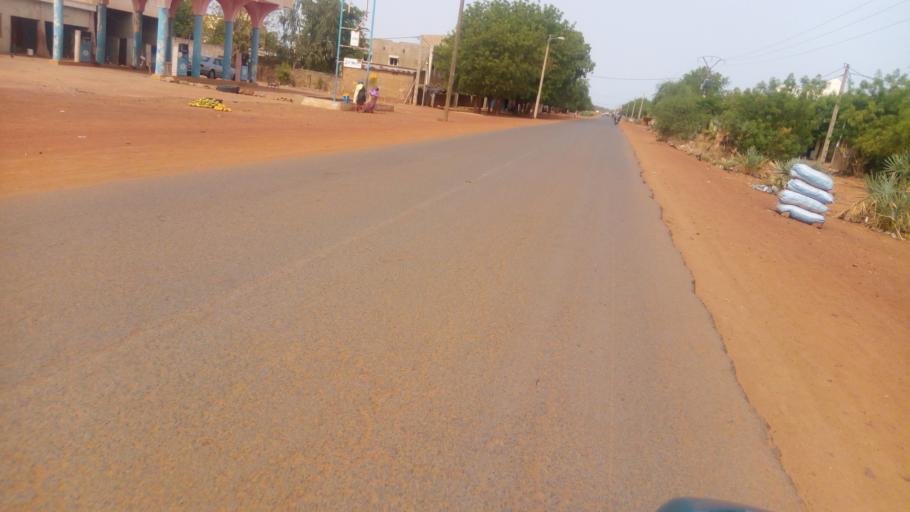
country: ML
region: Segou
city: Segou
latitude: 13.4326
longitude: -6.2955
